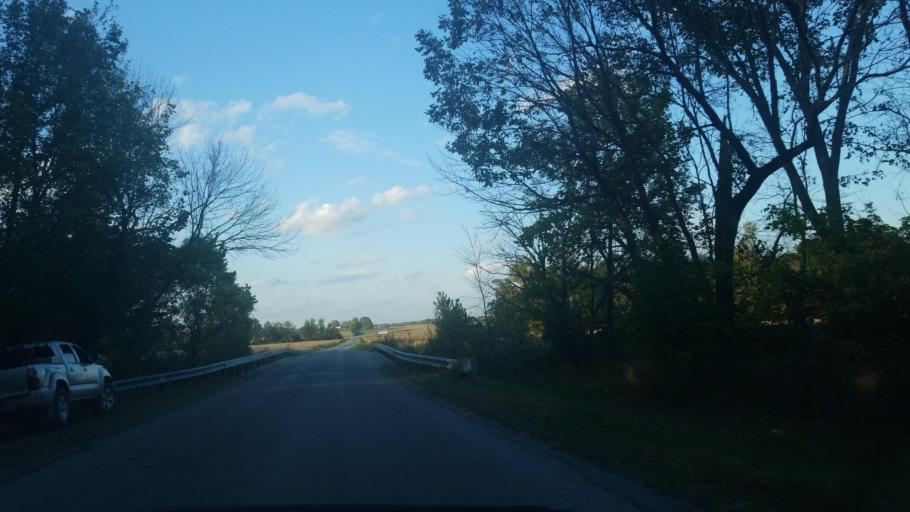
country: US
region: Illinois
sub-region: Saline County
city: Harrisburg
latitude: 37.8187
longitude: -88.6146
